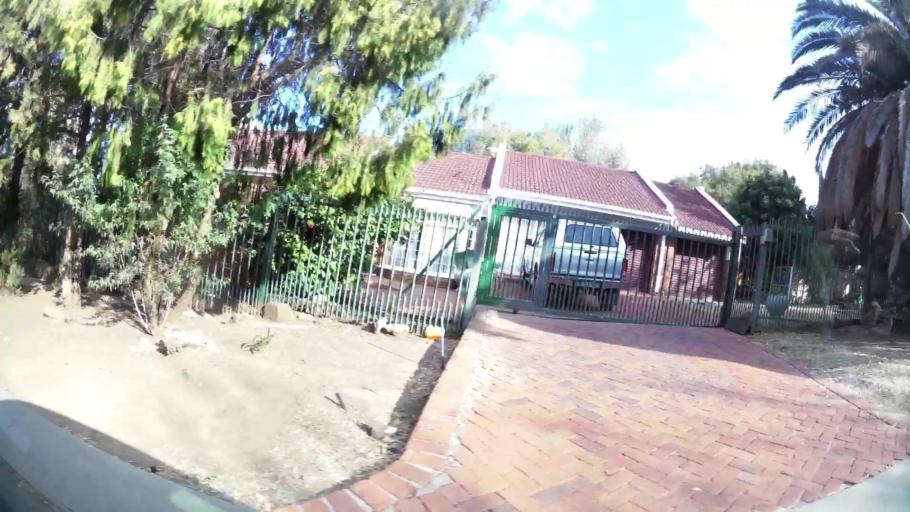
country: ZA
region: Orange Free State
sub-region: Mangaung Metropolitan Municipality
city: Bloemfontein
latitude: -29.0784
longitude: 26.2274
